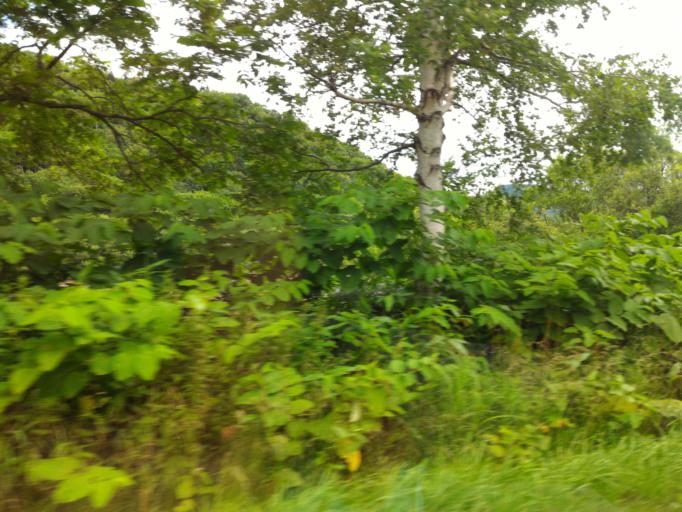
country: JP
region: Hokkaido
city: Nayoro
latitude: 44.7237
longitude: 142.2386
